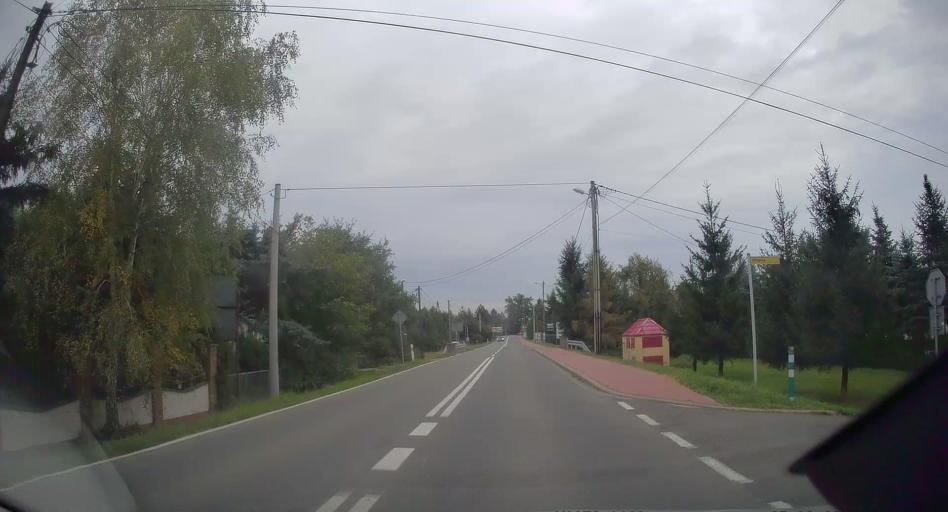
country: PL
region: Lesser Poland Voivodeship
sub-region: Powiat wielicki
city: Niepolomice
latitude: 50.0237
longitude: 20.1992
